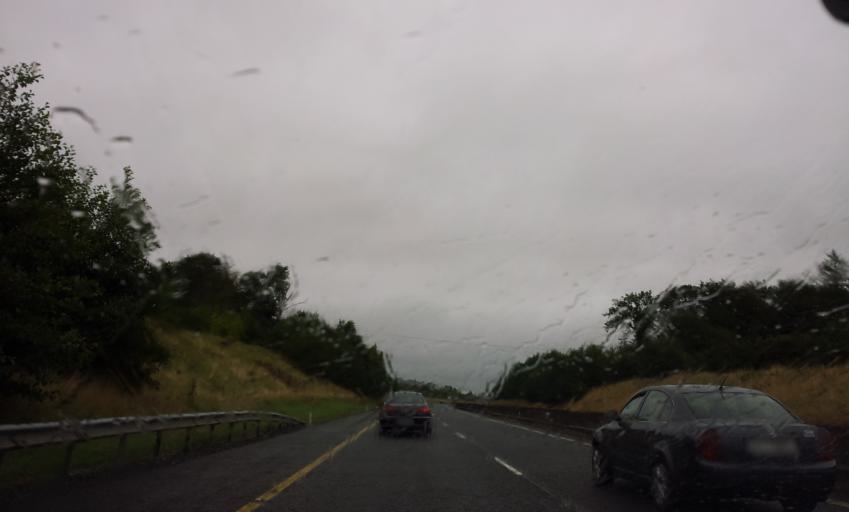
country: IE
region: Munster
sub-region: County Cork
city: Rathcormac
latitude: 52.0731
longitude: -8.3029
